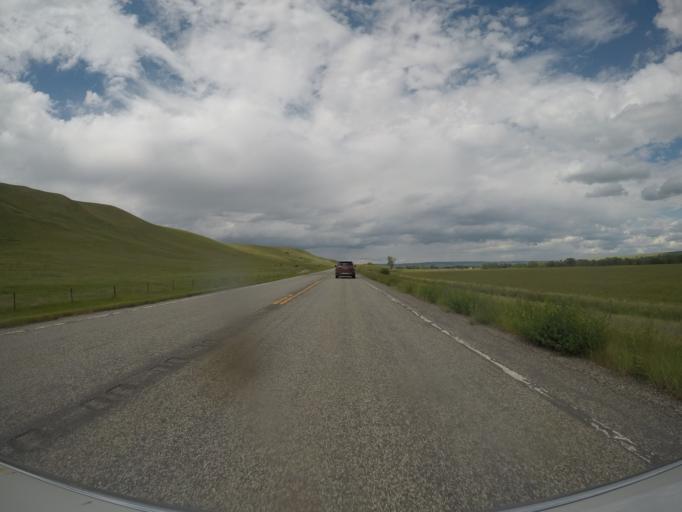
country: US
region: Montana
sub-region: Sweet Grass County
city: Big Timber
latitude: 45.7973
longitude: -109.9705
